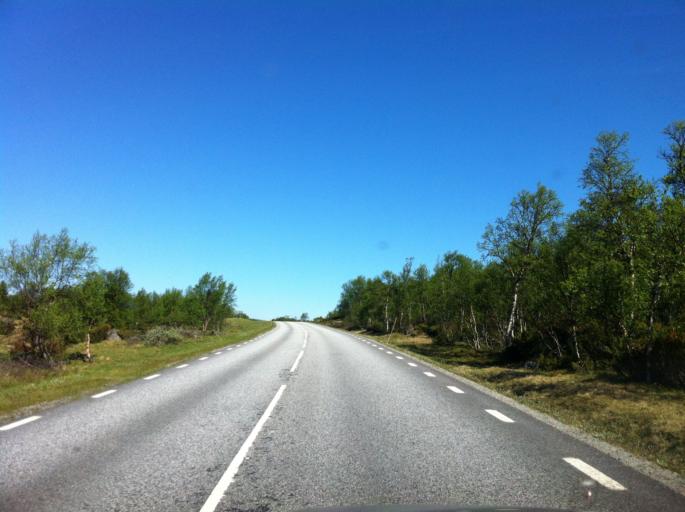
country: NO
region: Sor-Trondelag
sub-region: Tydal
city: Aas
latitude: 62.6194
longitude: 12.1344
